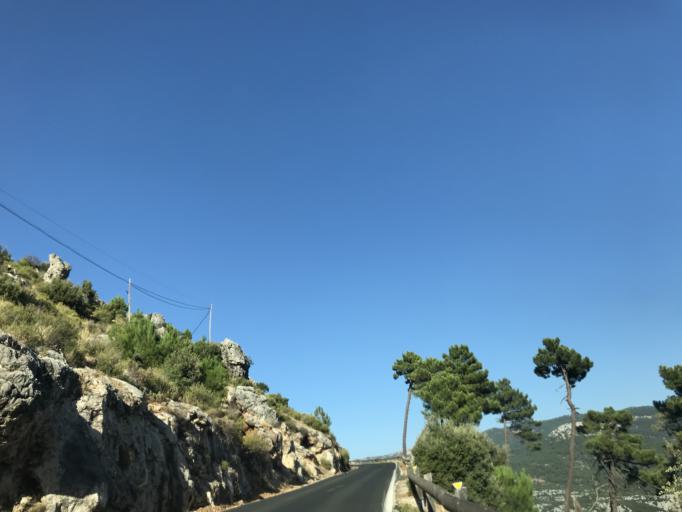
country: ES
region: Andalusia
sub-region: Provincia de Jaen
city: La Iruela
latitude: 37.9368
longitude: -2.9418
